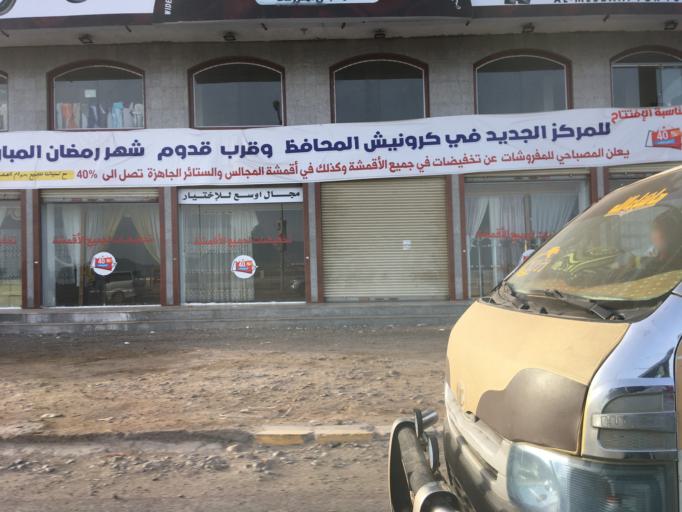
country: YE
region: Aden
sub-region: Ash Shaikh Outhman
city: Ash Shaykh `Uthman
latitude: 12.8591
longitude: 45.0068
